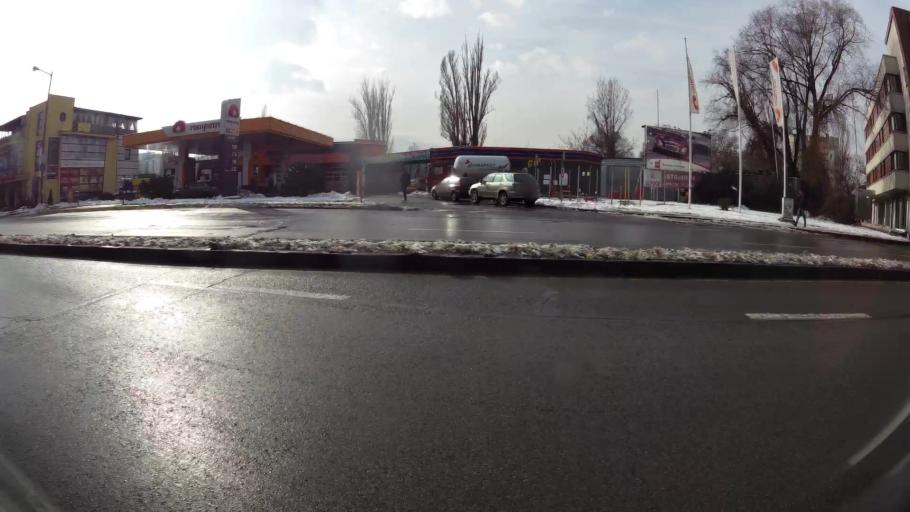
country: BG
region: Sofia-Capital
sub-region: Stolichna Obshtina
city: Sofia
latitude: 42.6995
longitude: 23.3606
